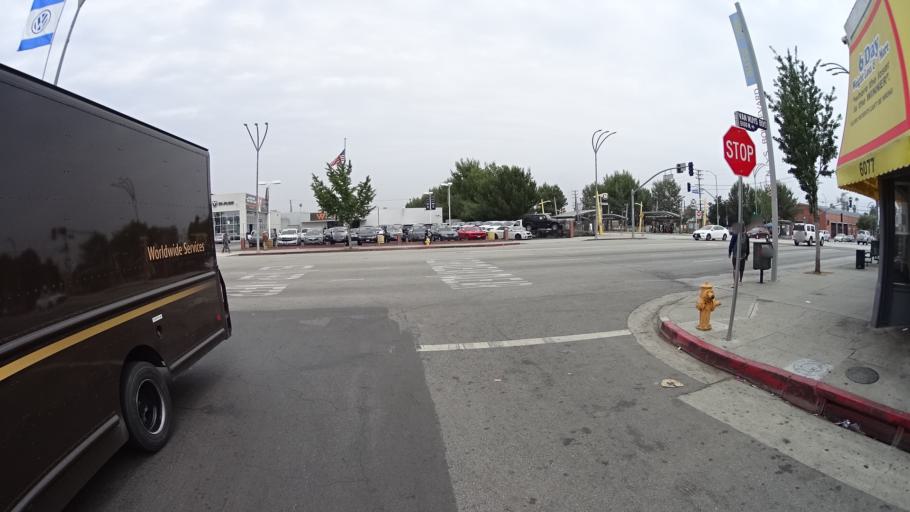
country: US
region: California
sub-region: Los Angeles County
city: Van Nuys
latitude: 34.1810
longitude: -118.4489
